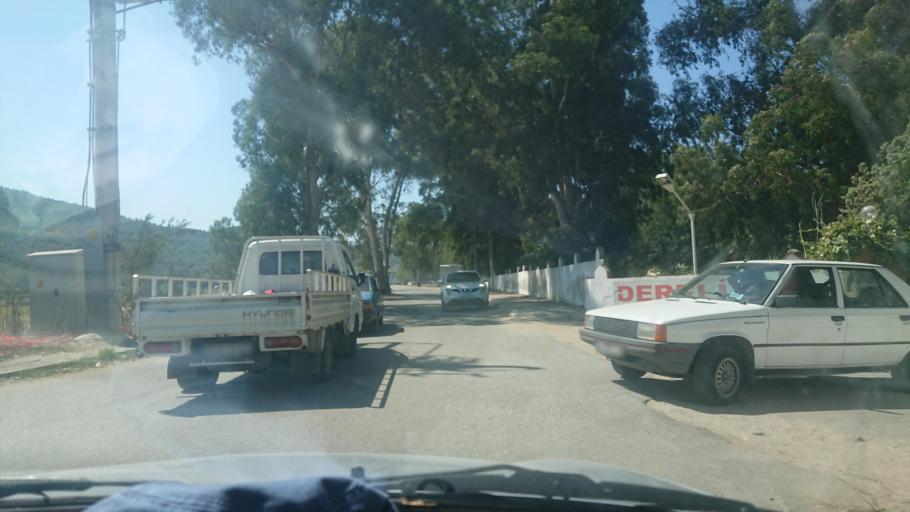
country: TR
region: Aydin
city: Kusadasi
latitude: 37.9405
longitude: 27.2770
